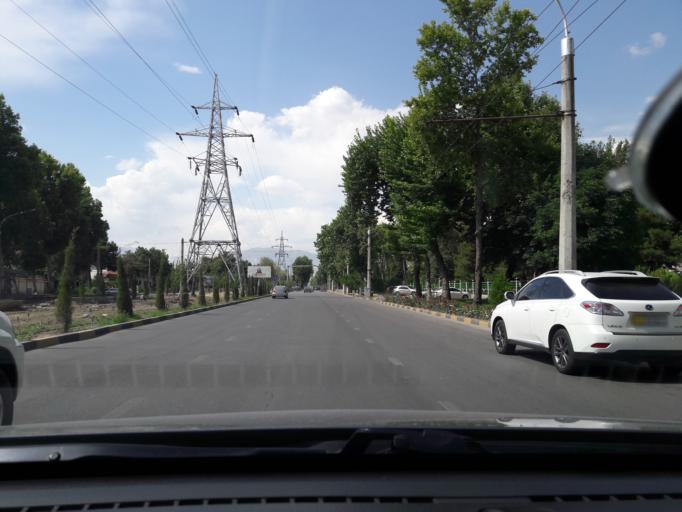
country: TJ
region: Dushanbe
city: Dushanbe
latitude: 38.5442
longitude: 68.7622
